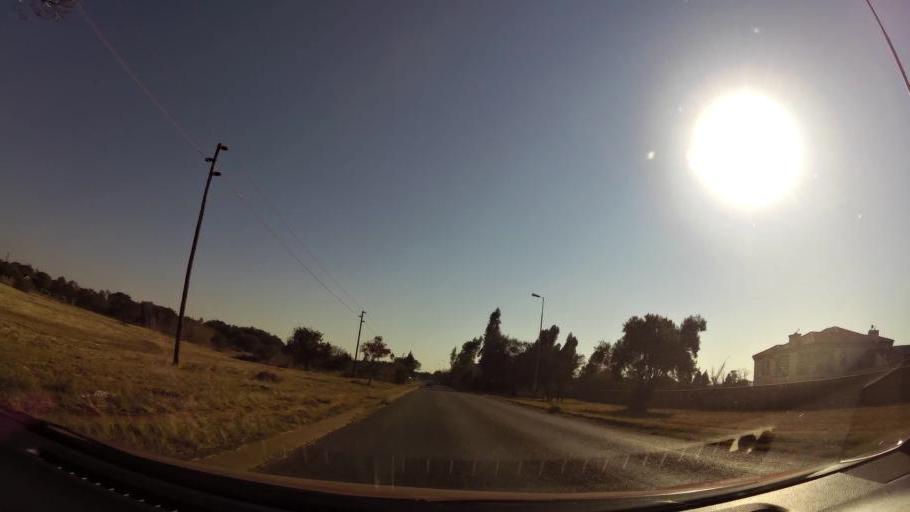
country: ZA
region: Gauteng
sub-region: City of Tshwane Metropolitan Municipality
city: Pretoria
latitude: -25.6629
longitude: 28.1320
